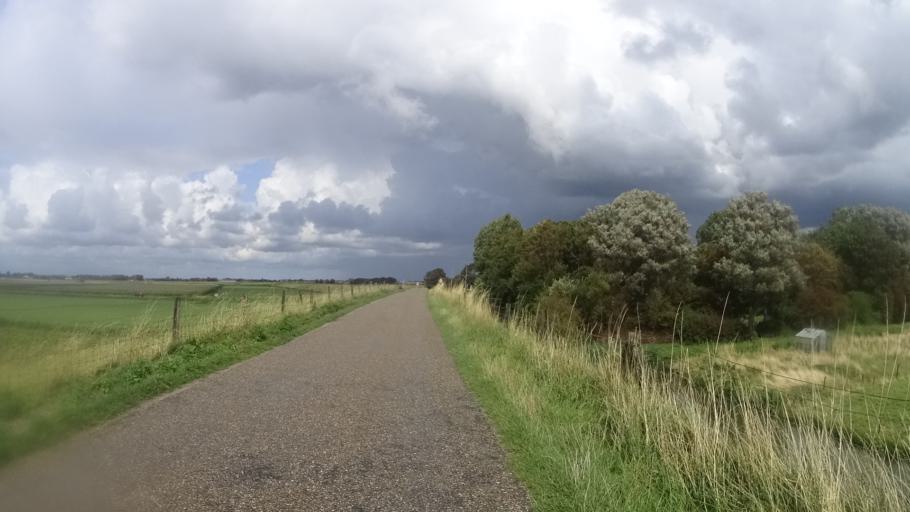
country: NL
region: North Holland
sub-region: Gemeente Schagen
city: Harenkarspel
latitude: 52.7741
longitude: 4.7400
